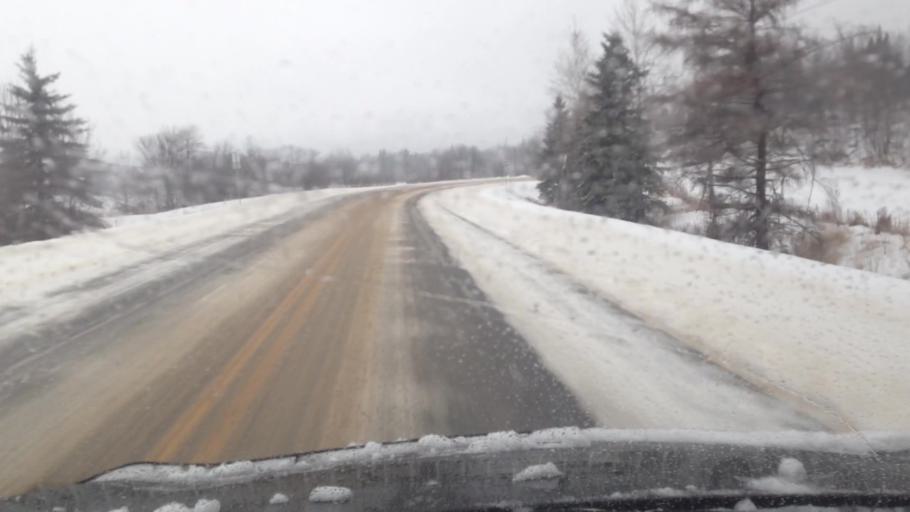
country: CA
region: Quebec
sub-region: Laurentides
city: Mont-Tremblant
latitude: 46.0701
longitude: -74.6217
